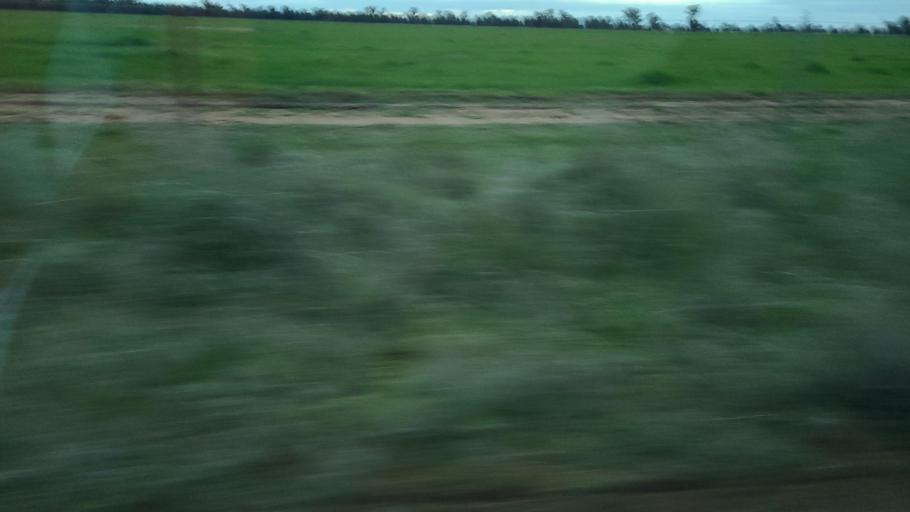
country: AU
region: New South Wales
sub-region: Coolamon
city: Coolamon
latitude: -34.8543
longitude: 146.9032
